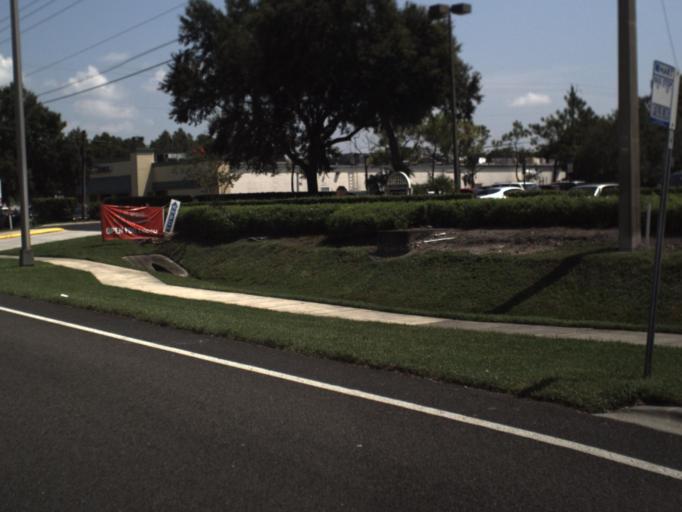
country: US
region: Florida
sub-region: Hillsborough County
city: Carrollwood Village
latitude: 28.0799
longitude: -82.5067
